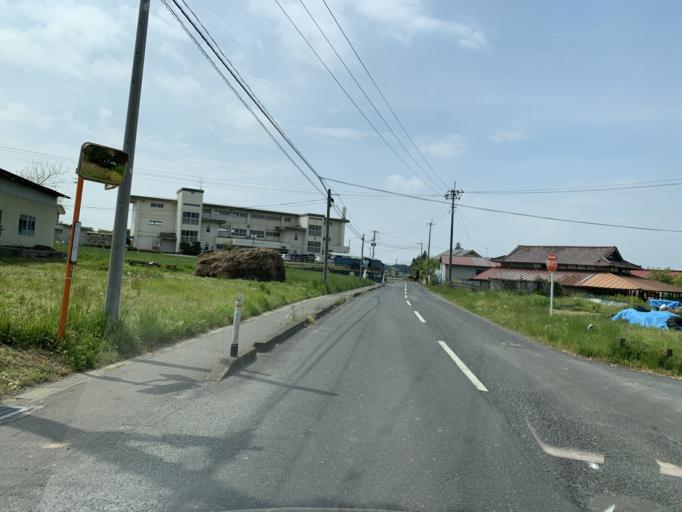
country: JP
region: Iwate
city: Ichinoseki
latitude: 38.8278
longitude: 141.2022
